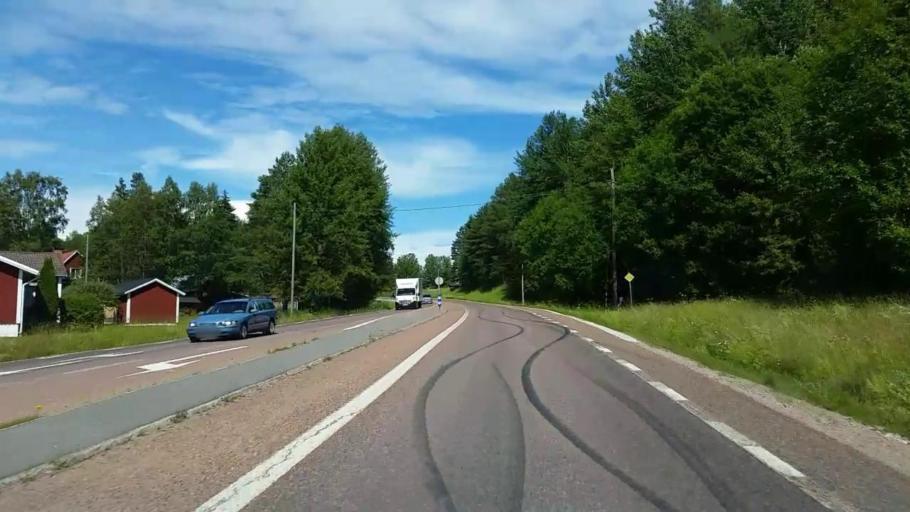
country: SE
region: Dalarna
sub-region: Rattviks Kommun
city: Raettvik
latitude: 61.0046
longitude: 15.2193
